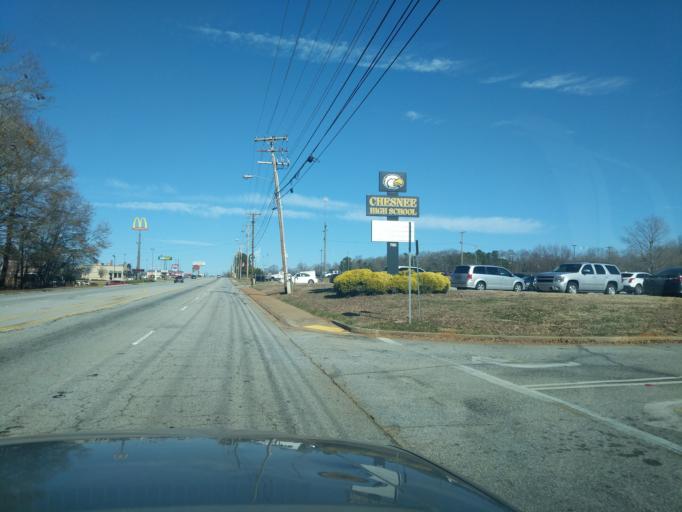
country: US
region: South Carolina
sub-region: Spartanburg County
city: Mayo
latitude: 35.1327
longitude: -81.8632
